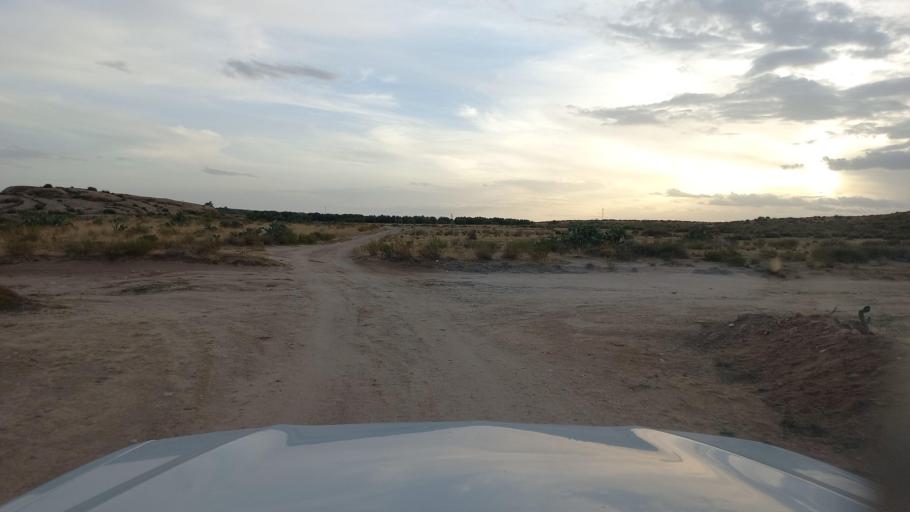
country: TN
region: Al Qasrayn
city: Sbiba
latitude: 35.4115
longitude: 9.0825
